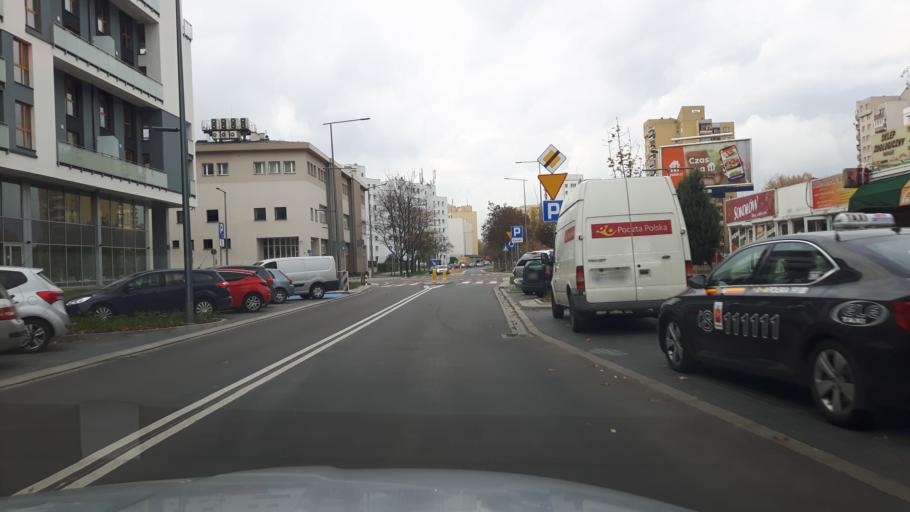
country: PL
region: Masovian Voivodeship
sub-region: Warszawa
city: Praga Polnoc
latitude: 52.2698
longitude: 21.0491
